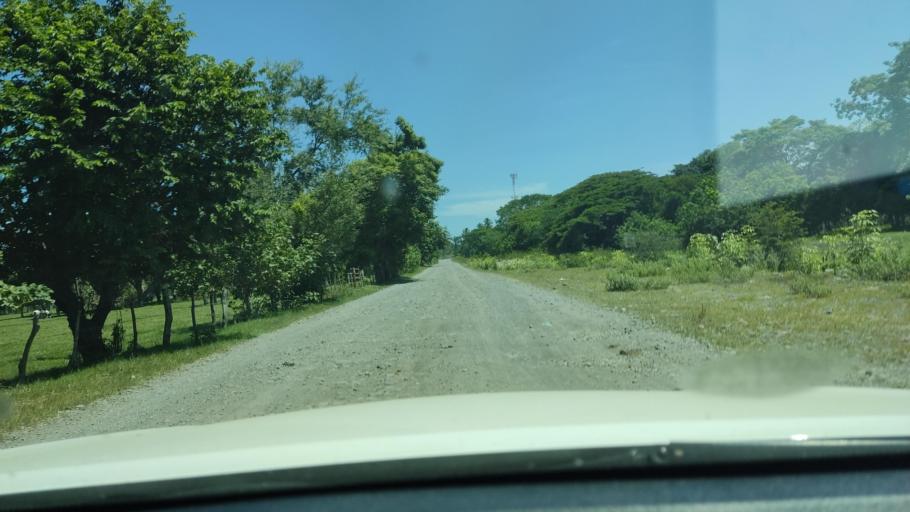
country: SV
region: Ahuachapan
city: San Francisco Menendez
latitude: 13.7563
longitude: -90.1197
